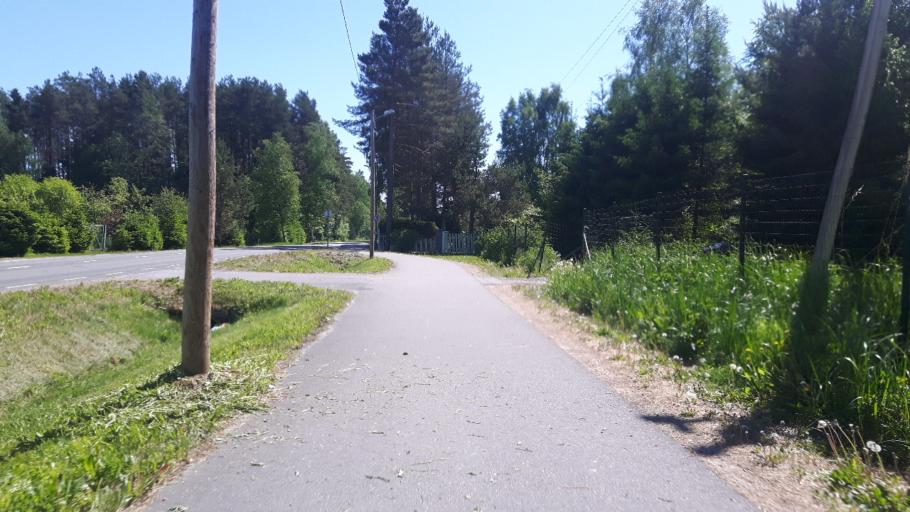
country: EE
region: Harju
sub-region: Saku vald
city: Saku
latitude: 59.2188
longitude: 24.6742
